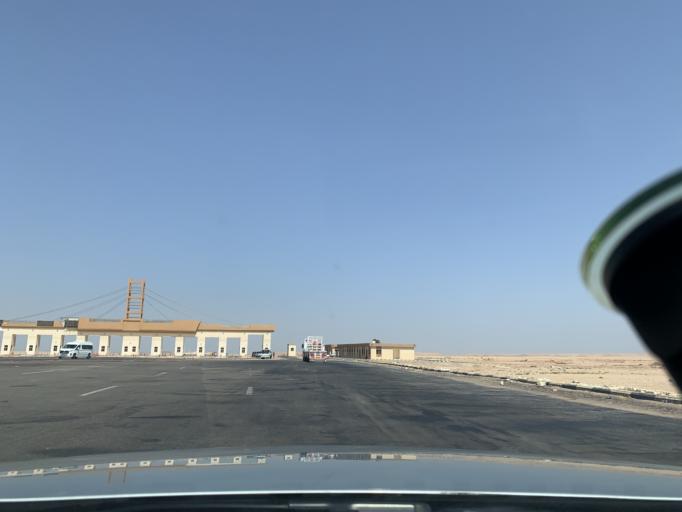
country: EG
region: As Suways
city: Ain Sukhna
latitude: 29.1104
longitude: 32.5478
